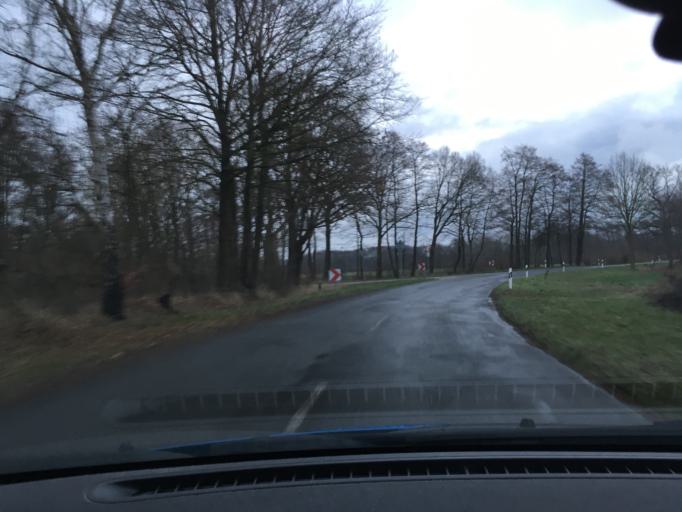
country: DE
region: Mecklenburg-Vorpommern
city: Nostorf
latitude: 53.4042
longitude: 10.6655
